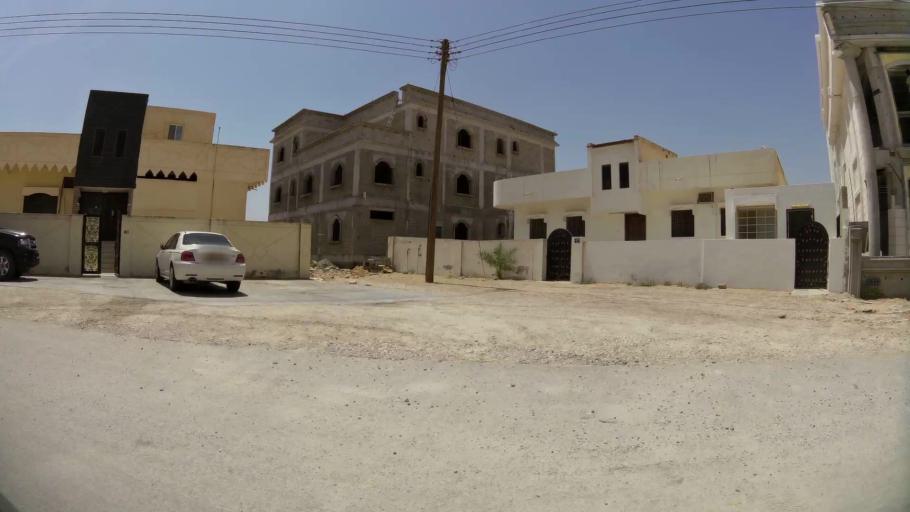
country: OM
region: Zufar
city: Salalah
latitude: 17.0653
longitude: 54.1565
